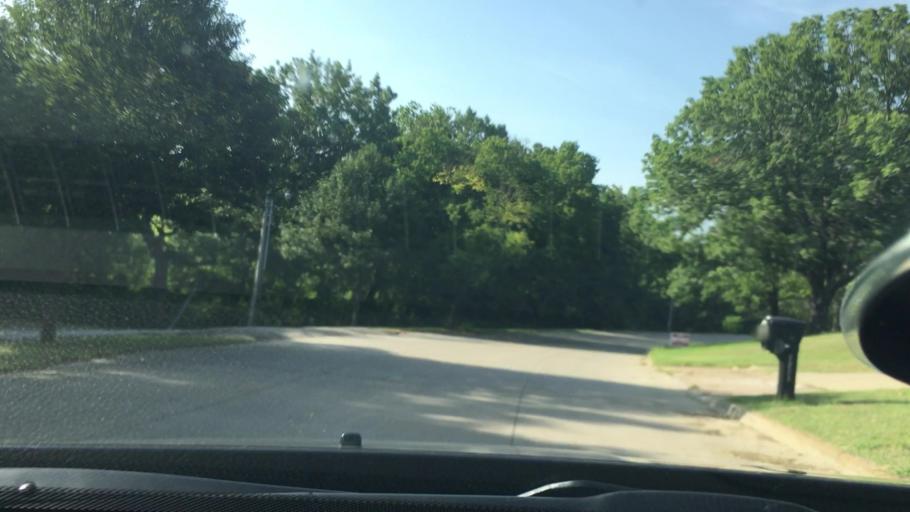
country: US
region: Oklahoma
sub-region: Pontotoc County
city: Ada
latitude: 34.7616
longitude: -96.6553
